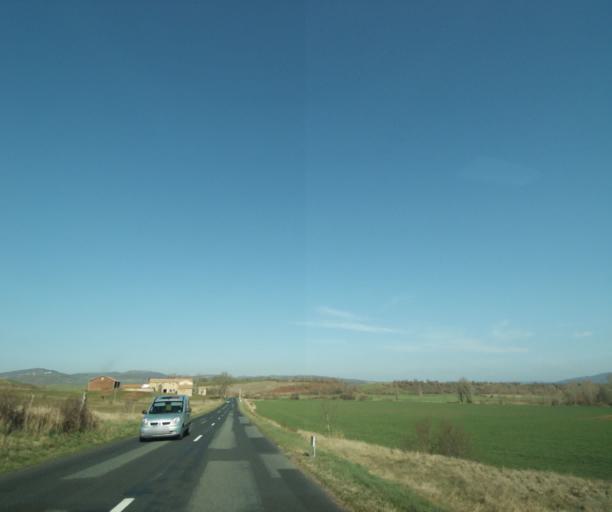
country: FR
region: Midi-Pyrenees
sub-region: Departement de l'Aveyron
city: Camares
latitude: 43.8669
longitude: 2.8236
